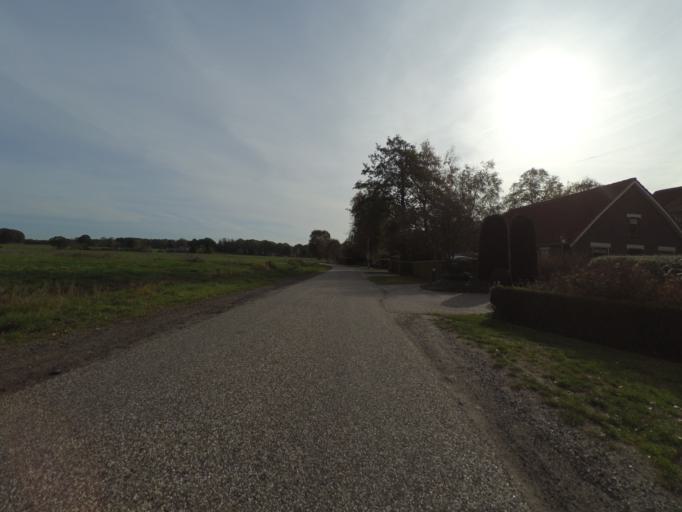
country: NL
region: Overijssel
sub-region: Gemeente Raalte
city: Raalte
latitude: 52.3555
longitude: 6.3777
